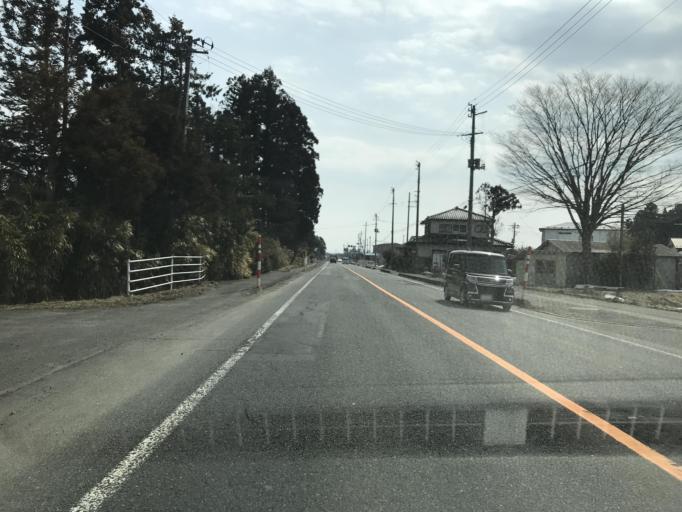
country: JP
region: Miyagi
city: Furukawa
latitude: 38.6871
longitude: 140.8526
